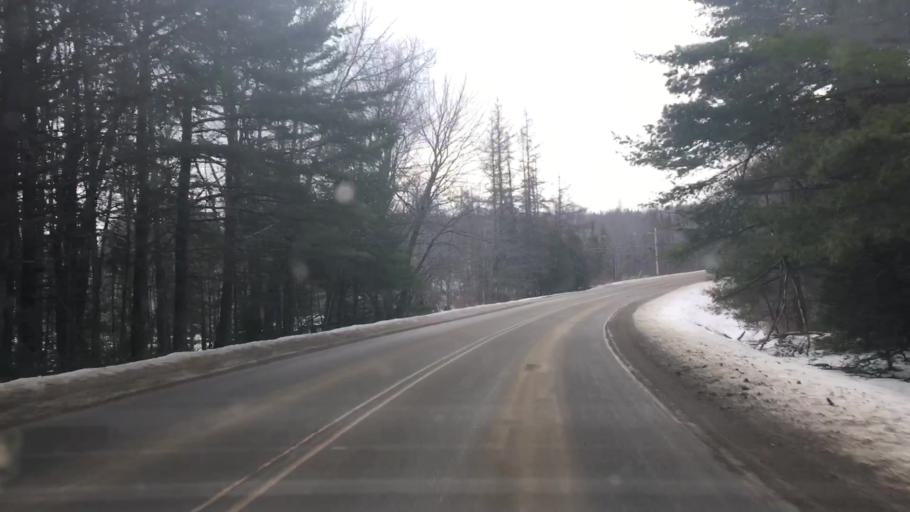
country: US
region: Maine
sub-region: Washington County
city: Calais
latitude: 45.0433
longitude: -67.3275
